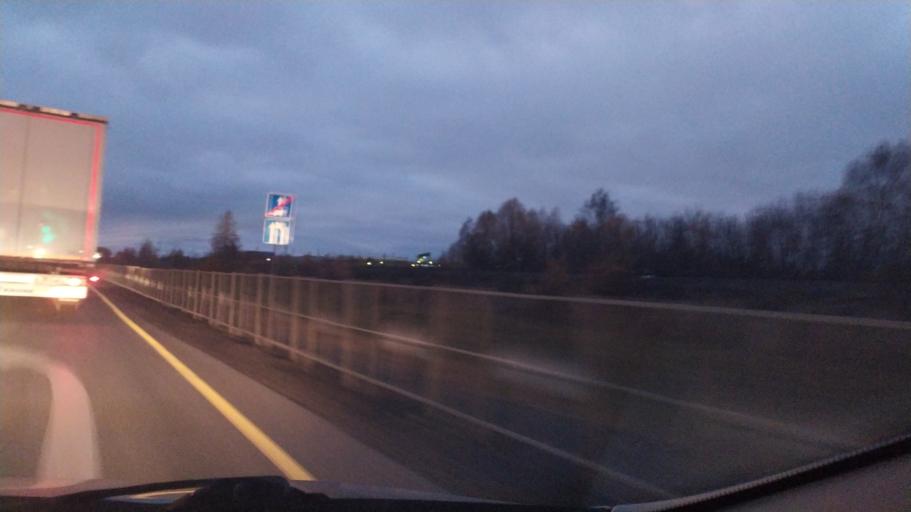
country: RU
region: Chuvashia
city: Novyye Lapsary
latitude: 56.0615
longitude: 47.2503
